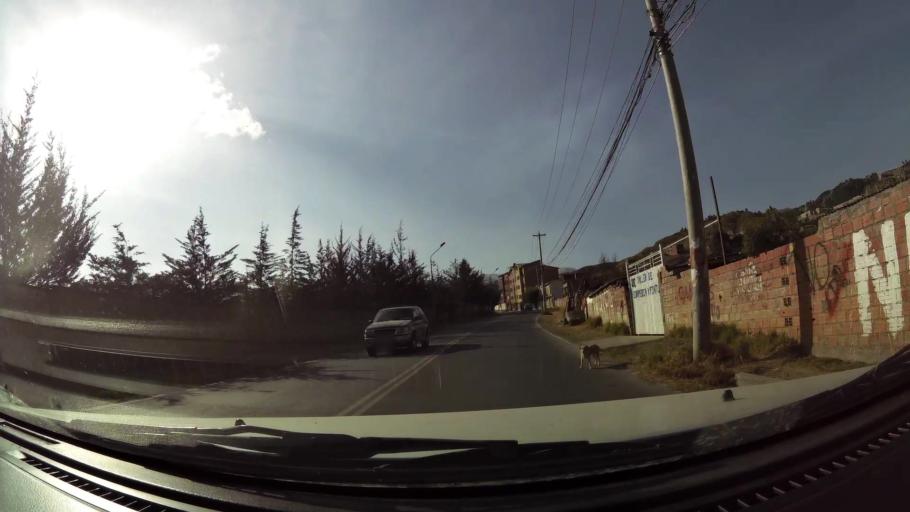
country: BO
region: La Paz
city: La Paz
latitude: -16.5237
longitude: -68.0803
